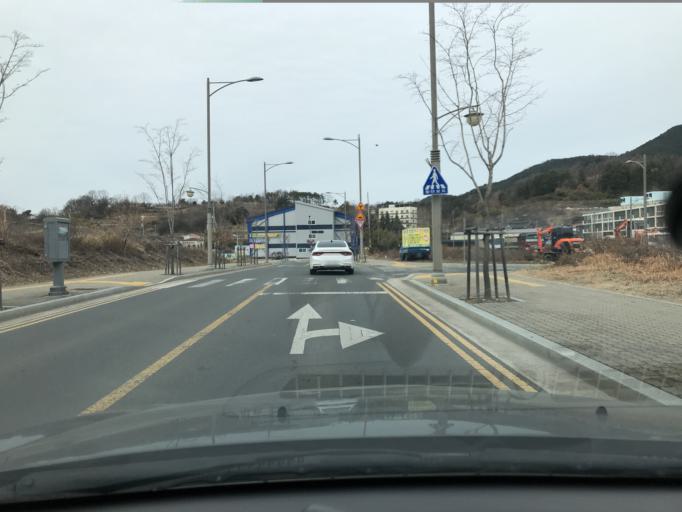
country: KR
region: Daegu
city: Hwawon
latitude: 35.6991
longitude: 128.4534
